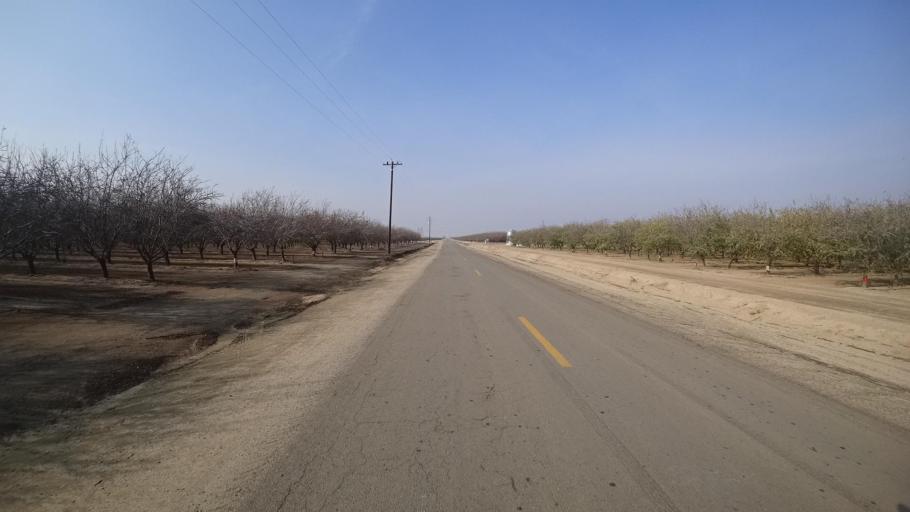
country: US
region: California
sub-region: Kern County
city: Lebec
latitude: 34.9930
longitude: -118.8537
